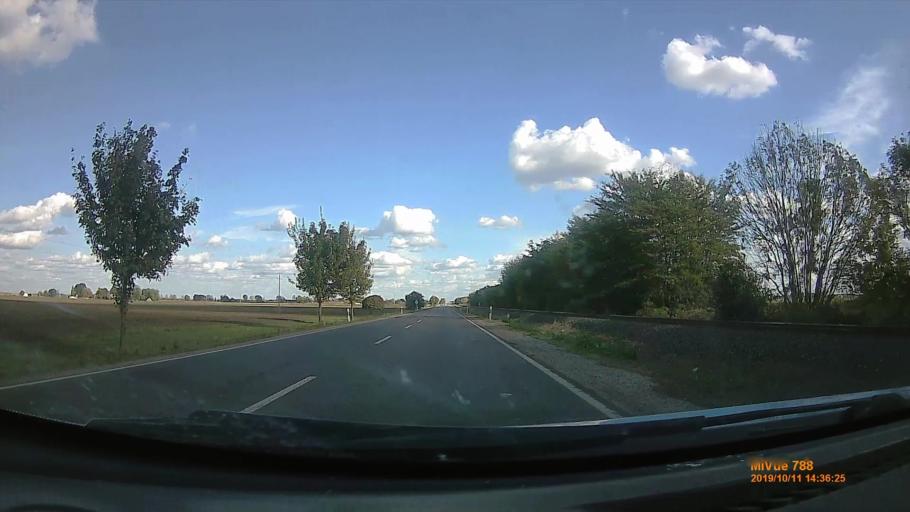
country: HU
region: Hajdu-Bihar
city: Ebes
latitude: 47.5571
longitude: 21.5082
